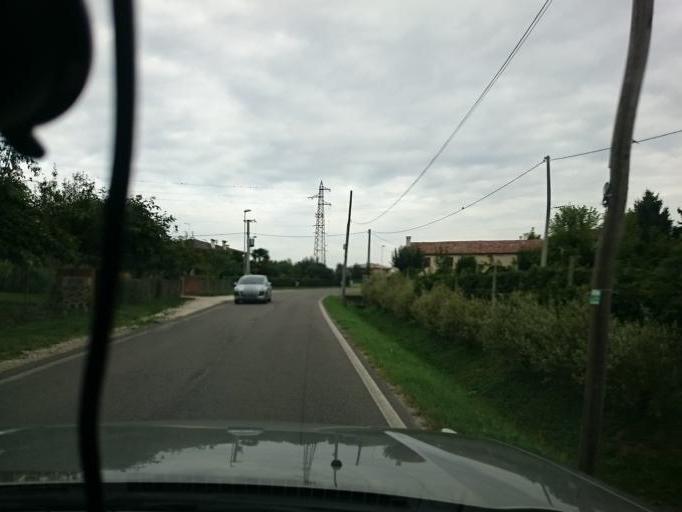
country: IT
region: Veneto
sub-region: Provincia di Padova
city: Saccolongo
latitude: 45.4209
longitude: 11.7493
